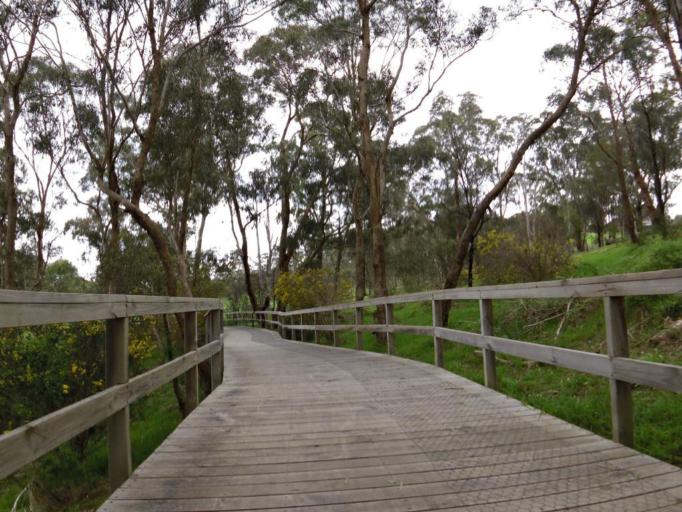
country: AU
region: Victoria
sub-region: Nillumbik
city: Eltham
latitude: -37.7391
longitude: 145.1622
